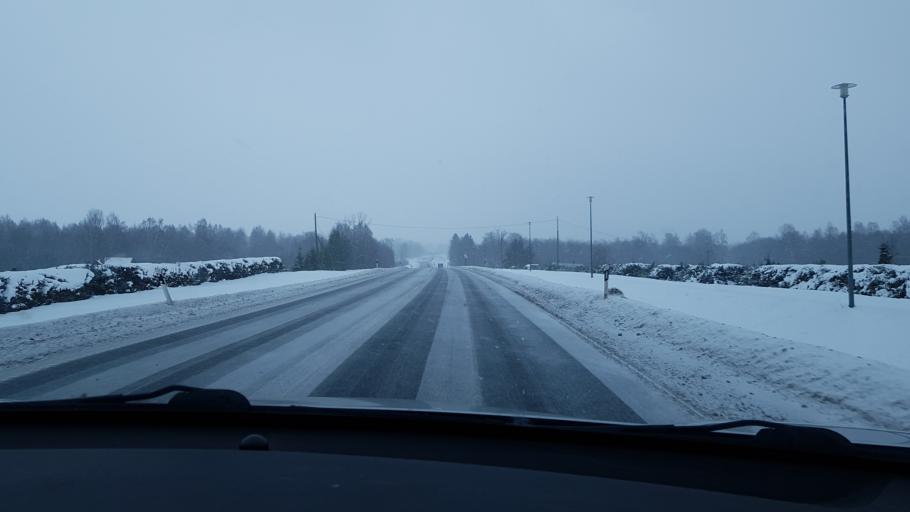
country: EE
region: Jaervamaa
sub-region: Tueri vald
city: Tueri
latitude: 58.8403
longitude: 25.4750
